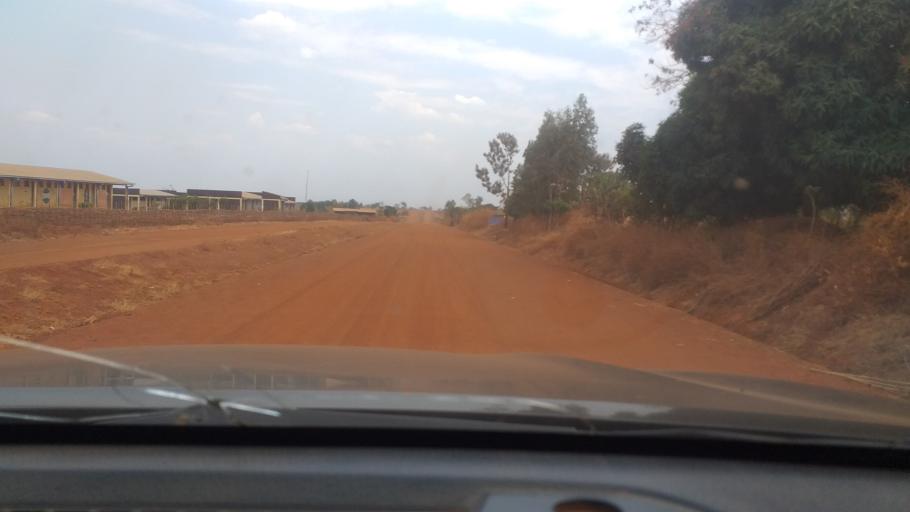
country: ET
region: Binshangul Gumuz
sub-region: Asosa
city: Asosa
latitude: 10.0681
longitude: 34.6781
